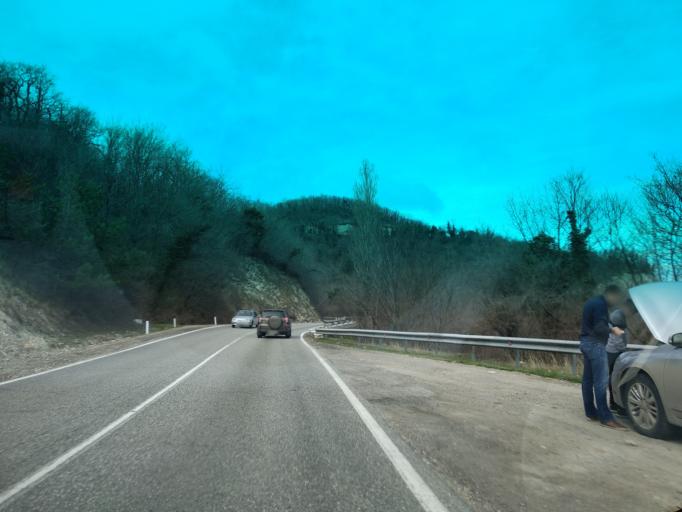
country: RU
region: Krasnodarskiy
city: Shepsi
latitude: 44.0662
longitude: 39.1371
